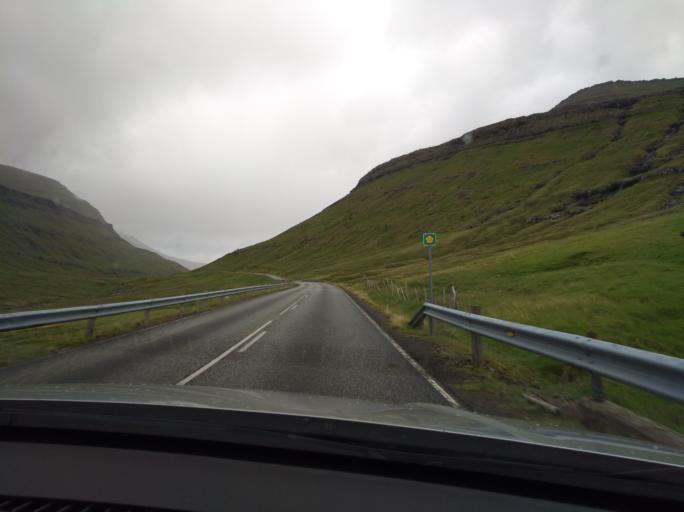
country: FO
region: Eysturoy
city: Fuglafjordur
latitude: 62.2255
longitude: -6.8798
